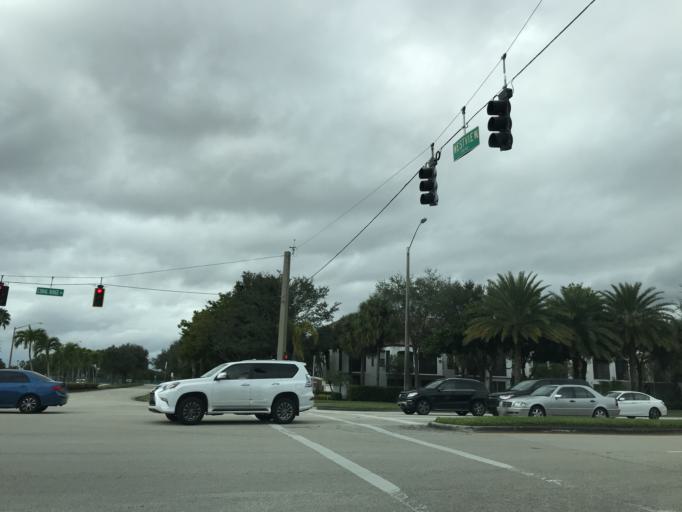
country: US
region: Florida
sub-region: Broward County
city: Coral Springs
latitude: 26.2974
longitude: -80.2788
